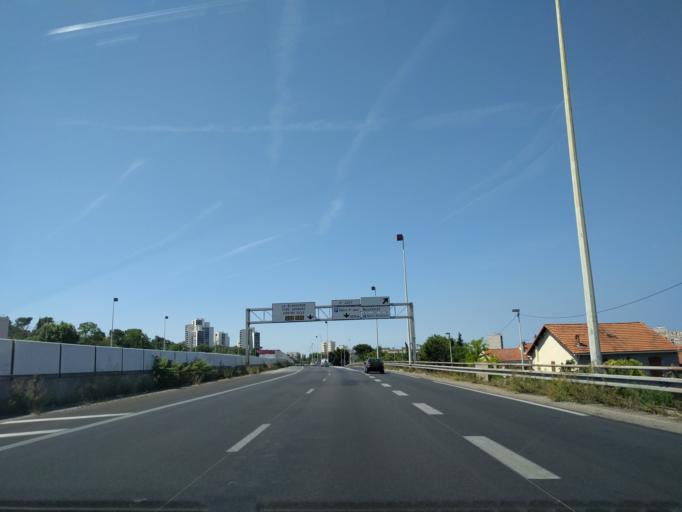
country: FR
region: Provence-Alpes-Cote d'Azur
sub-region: Departement des Bouches-du-Rhone
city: Marseille 13
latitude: 43.3227
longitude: 5.4182
